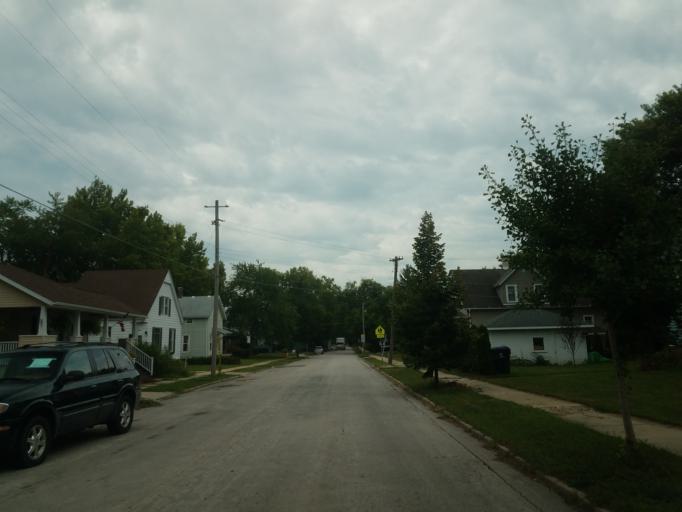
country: US
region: Illinois
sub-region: McLean County
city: Bloomington
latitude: 40.4770
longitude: -88.9751
